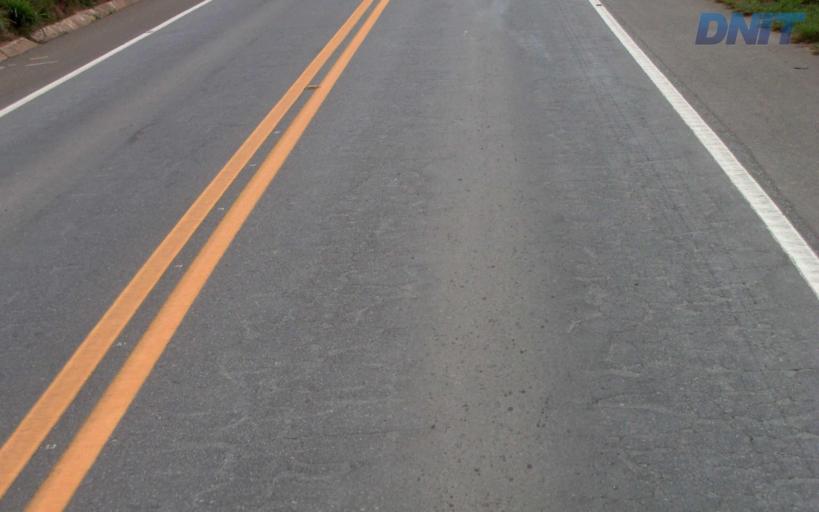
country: BR
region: Minas Gerais
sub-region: Governador Valadares
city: Governador Valadares
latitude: -18.9540
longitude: -42.0738
